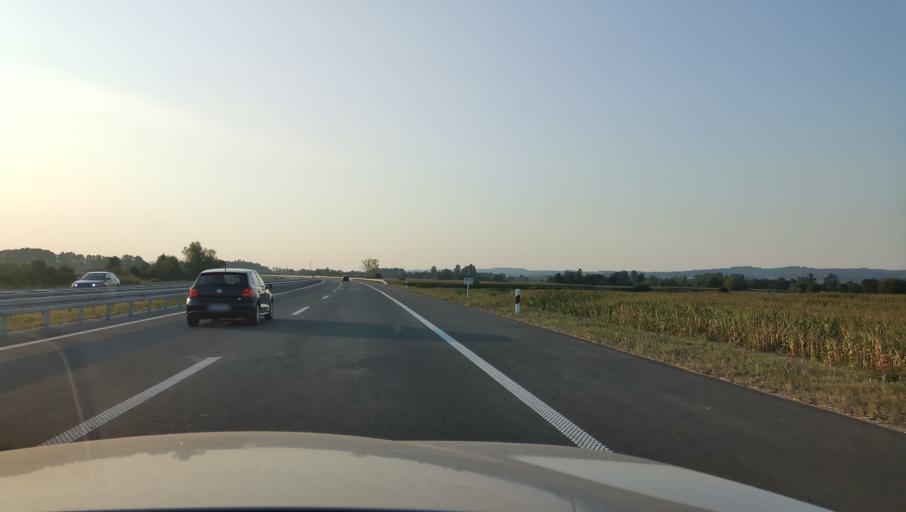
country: RS
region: Central Serbia
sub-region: Kolubarski Okrug
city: Ljig
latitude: 44.2769
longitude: 20.2640
